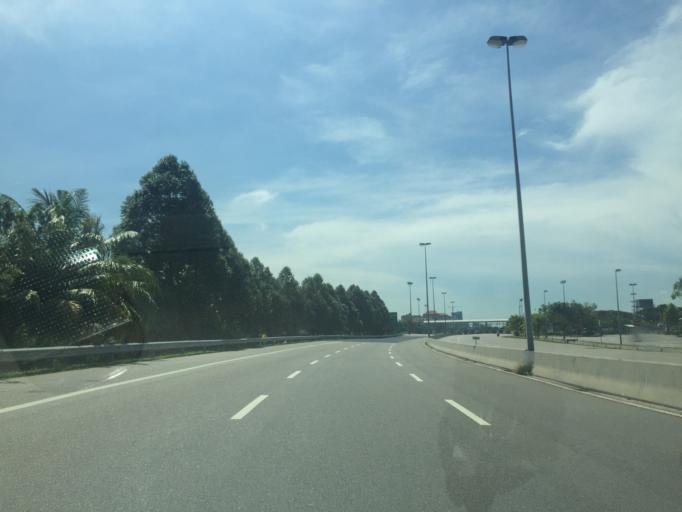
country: MY
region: Penang
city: Permatang Kuching
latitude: 5.4355
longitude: 100.3781
